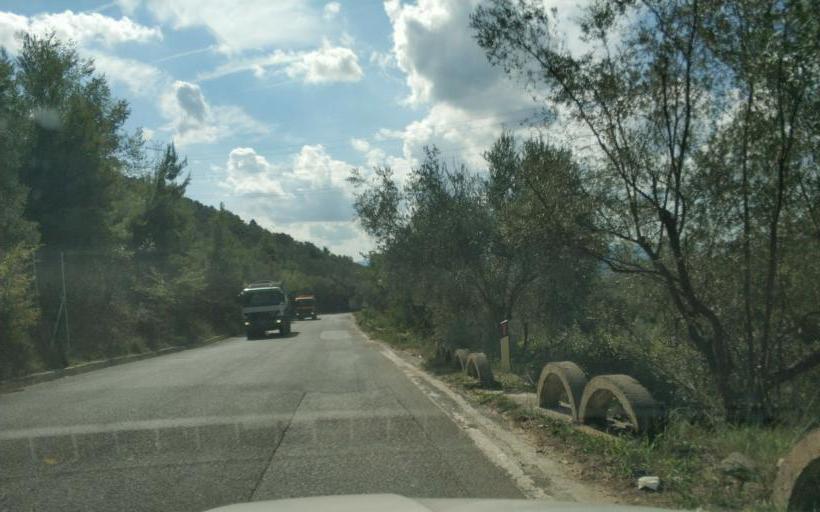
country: AL
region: Durres
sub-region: Rrethi i Krujes
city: Kruje
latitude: 41.4866
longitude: 19.7671
